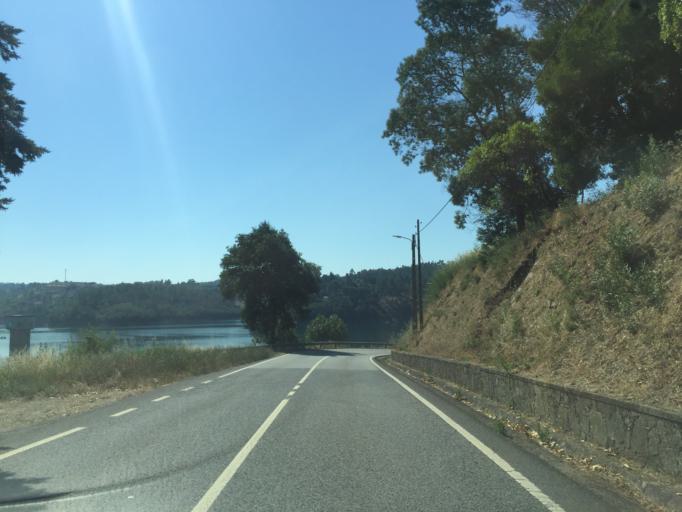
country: PT
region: Santarem
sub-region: Constancia
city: Constancia
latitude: 39.5453
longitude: -8.3209
